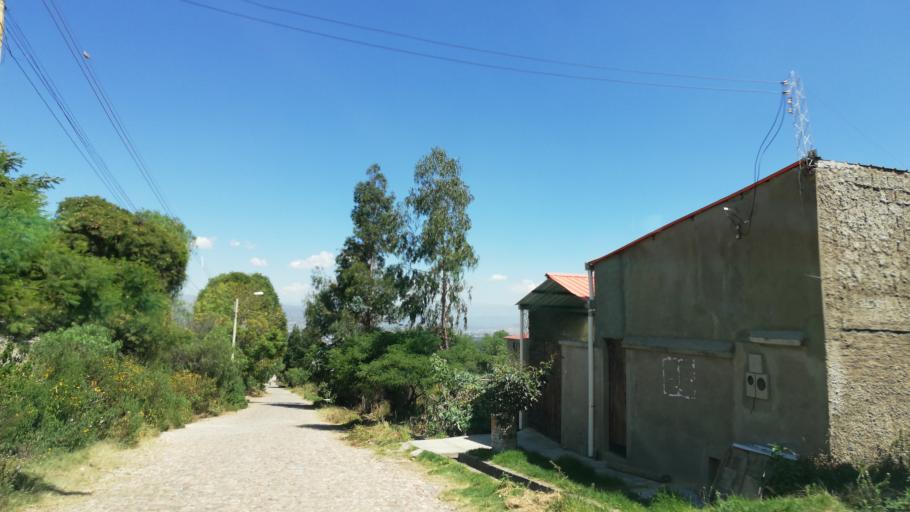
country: BO
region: Cochabamba
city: Cochabamba
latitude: -17.3233
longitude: -66.2128
